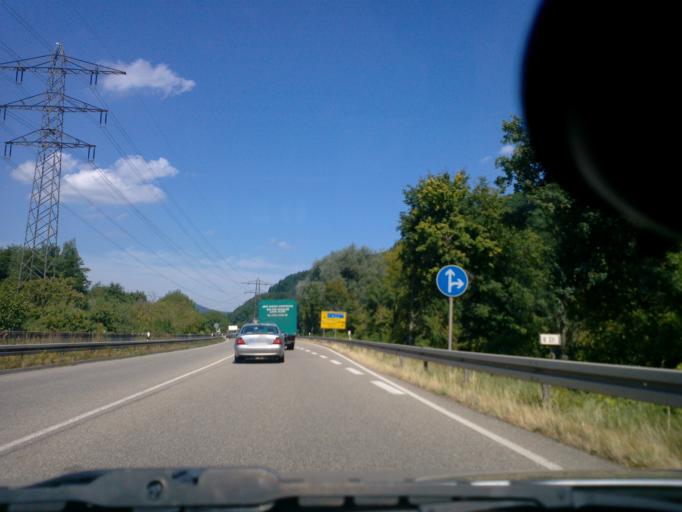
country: DE
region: Baden-Wuerttemberg
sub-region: Freiburg Region
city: Steinach
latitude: 48.3055
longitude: 8.0604
